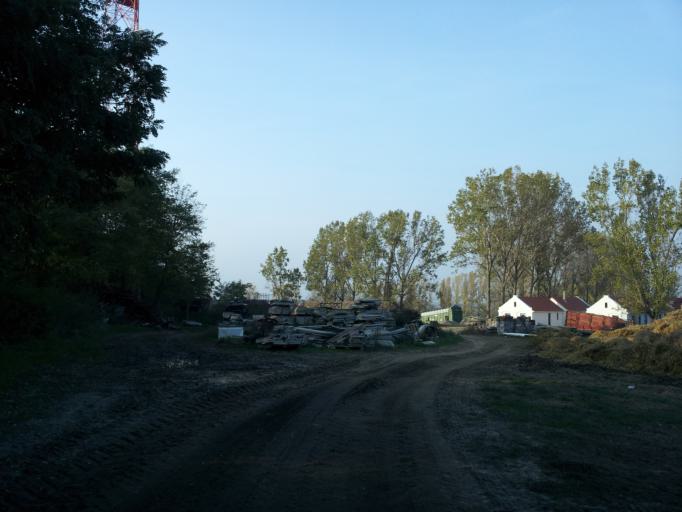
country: HU
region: Komarom-Esztergom
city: Kisber
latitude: 47.4877
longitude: 18.0447
